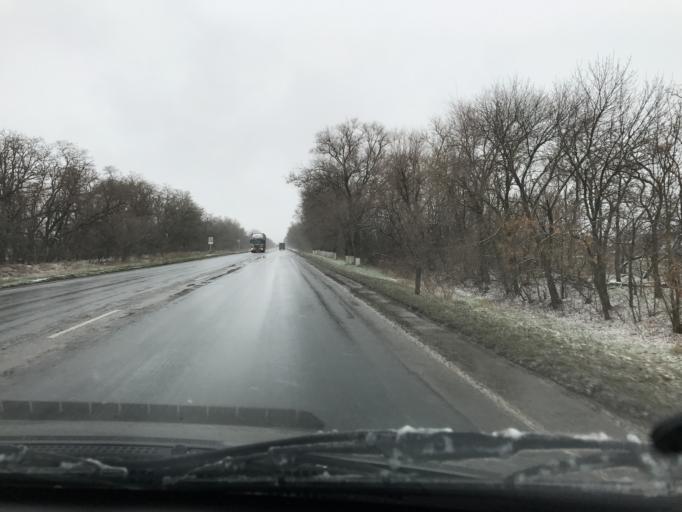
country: RU
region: Rostov
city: Zernograd
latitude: 46.8103
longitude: 40.3066
